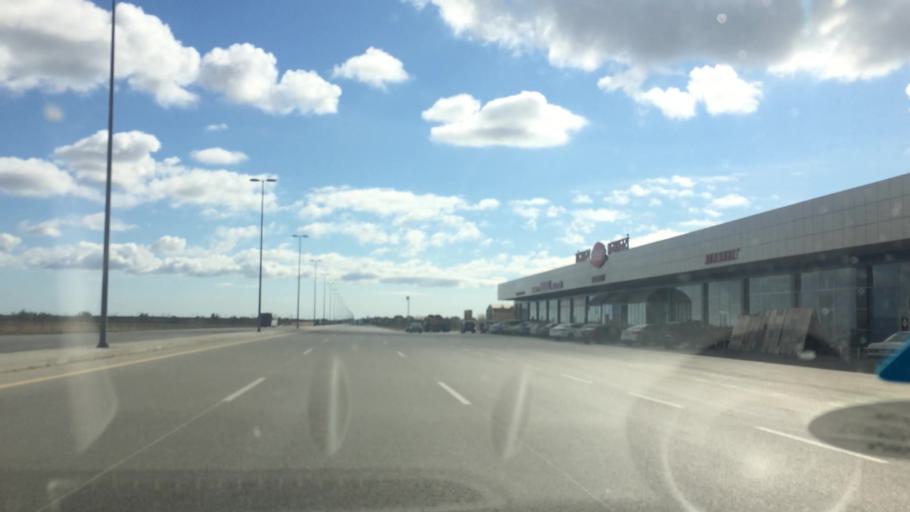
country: AZ
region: Baki
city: Qala
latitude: 40.4564
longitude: 50.1422
